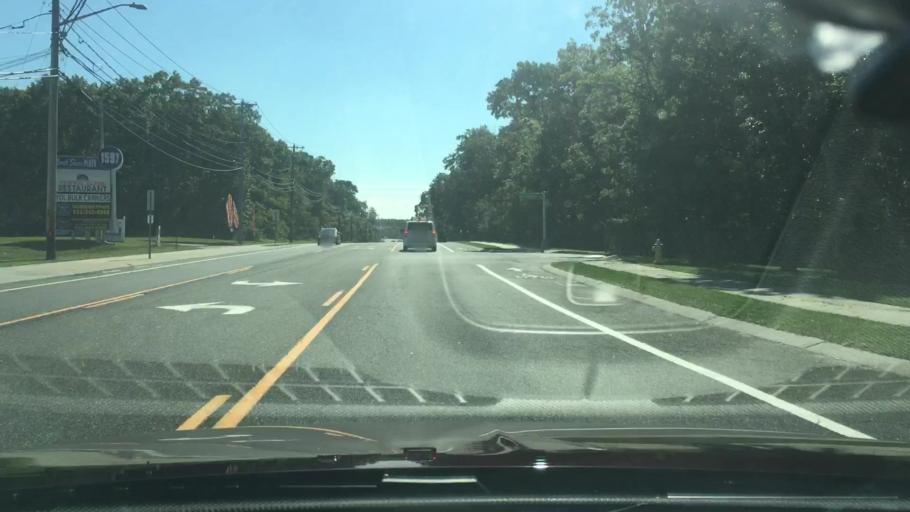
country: US
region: New York
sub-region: Suffolk County
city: Port Jefferson Station
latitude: 40.9095
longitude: -73.0290
